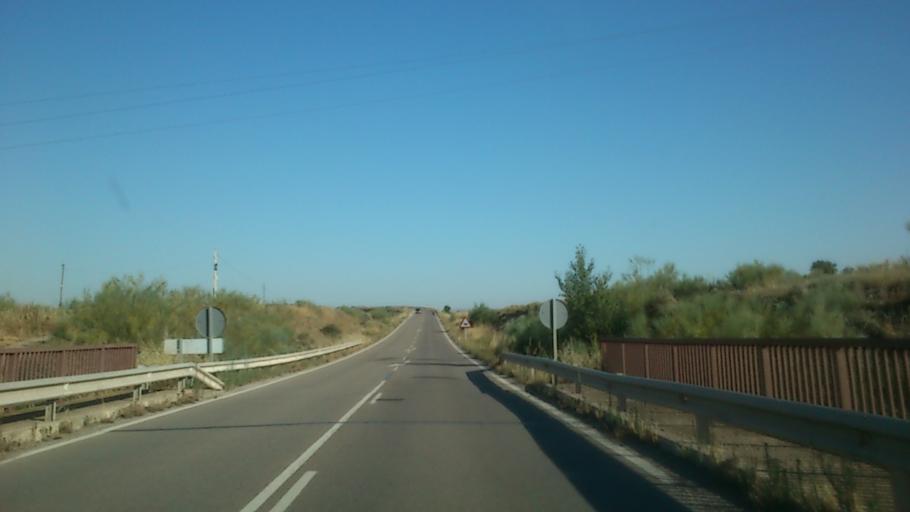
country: ES
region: Aragon
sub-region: Provincia de Zaragoza
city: San Mateo de Gallego
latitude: 41.8229
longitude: -0.7846
